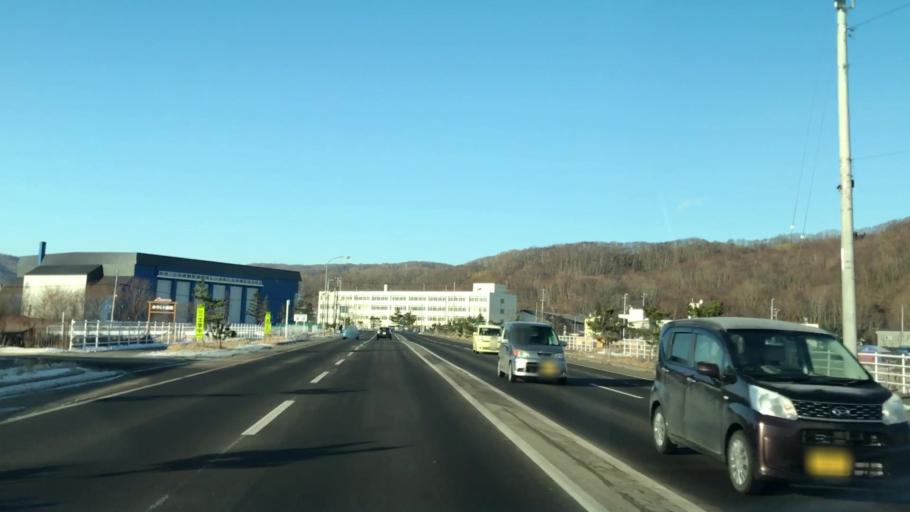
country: JP
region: Hokkaido
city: Muroran
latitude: 42.3928
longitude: 141.0822
